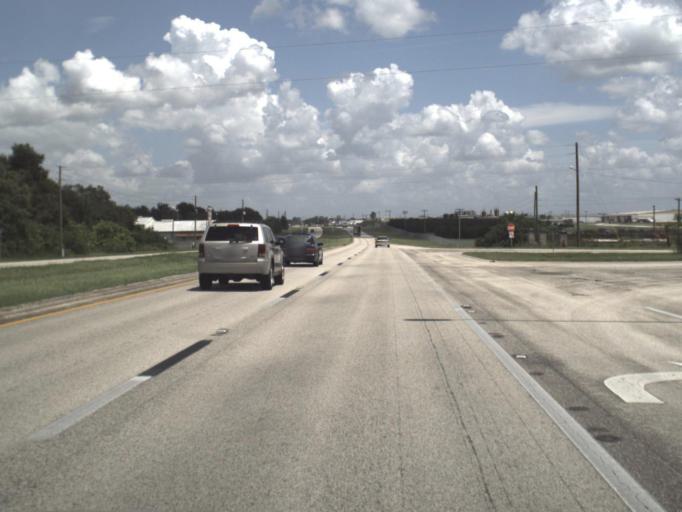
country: US
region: Florida
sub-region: Polk County
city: Eagle Lake
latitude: 27.9444
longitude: -81.7976
